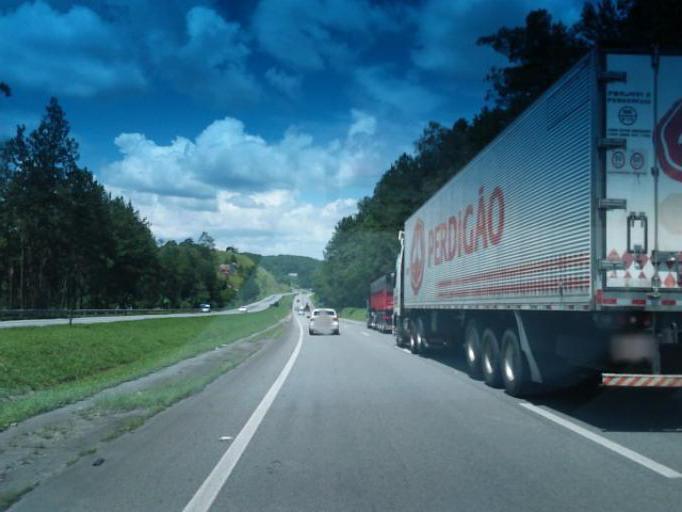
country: BR
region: Sao Paulo
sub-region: Juquitiba
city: Juquitiba
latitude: -23.9390
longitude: -47.0876
